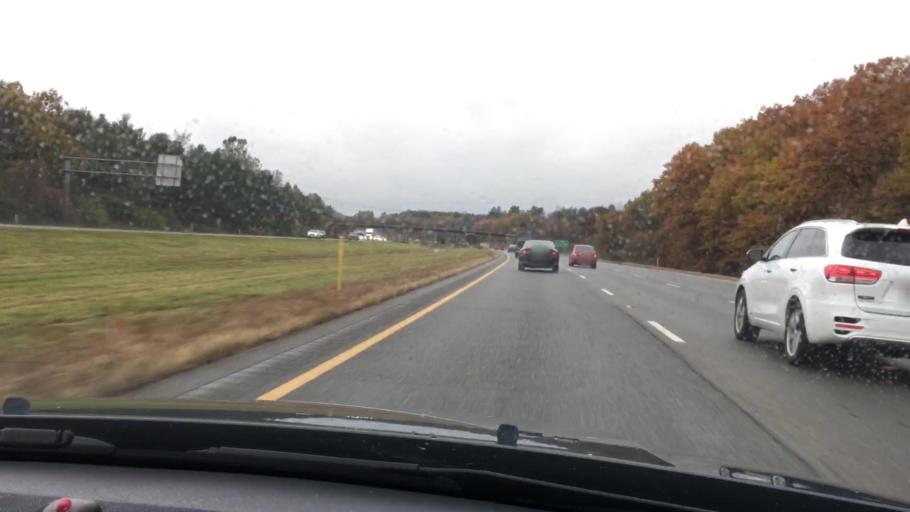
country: US
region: Massachusetts
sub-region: Middlesex County
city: Littleton Common
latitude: 42.5475
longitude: -71.4834
